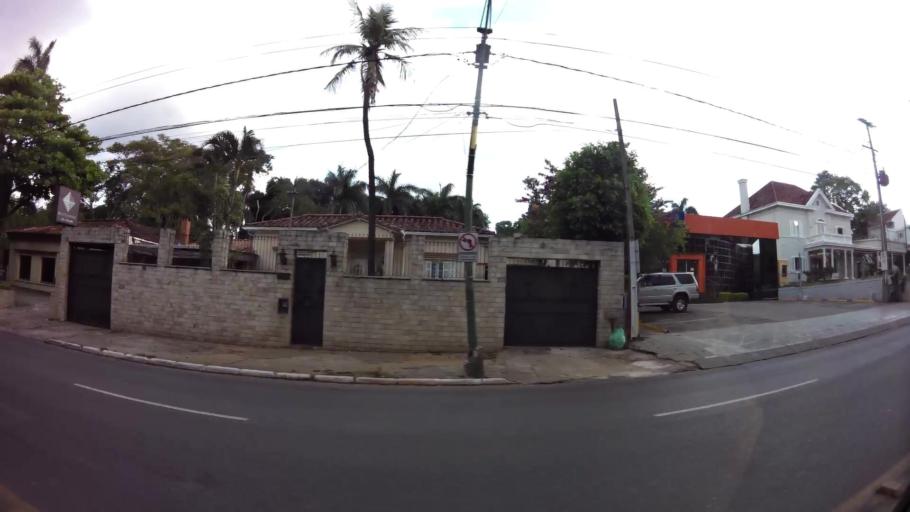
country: PY
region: Asuncion
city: Asuncion
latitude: -25.2909
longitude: -57.5945
